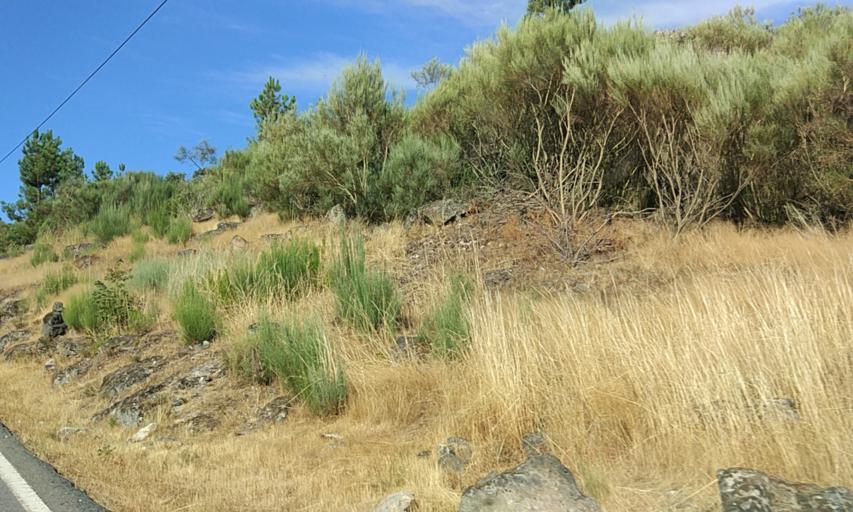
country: PT
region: Vila Real
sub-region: Sabrosa
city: Sabrosa
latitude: 41.3743
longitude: -7.5591
